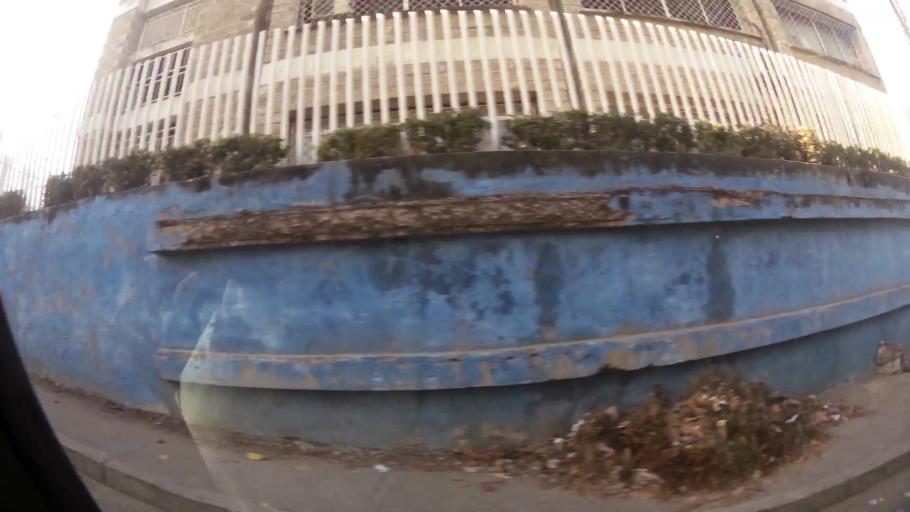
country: CO
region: Bolivar
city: Cartagena
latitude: 10.4048
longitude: -75.5080
